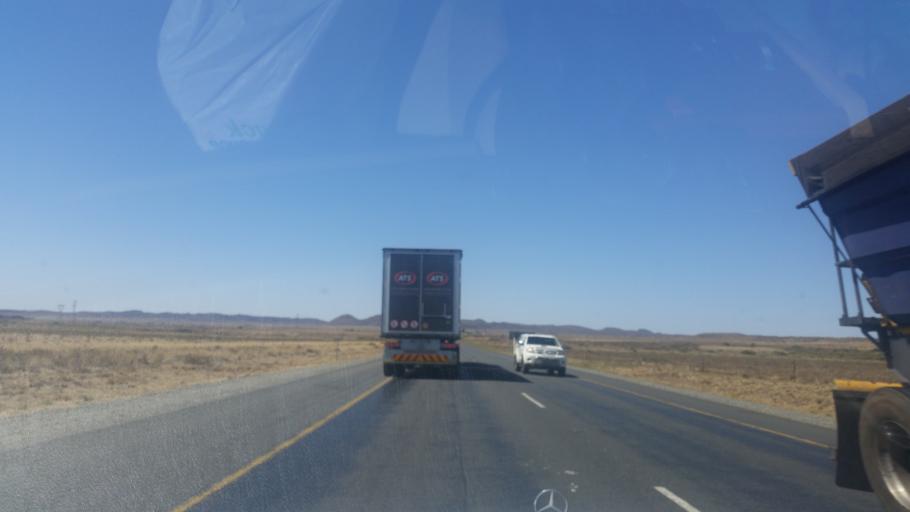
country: ZA
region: Northern Cape
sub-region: Pixley ka Seme District Municipality
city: Colesberg
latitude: -30.6982
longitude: 25.1303
